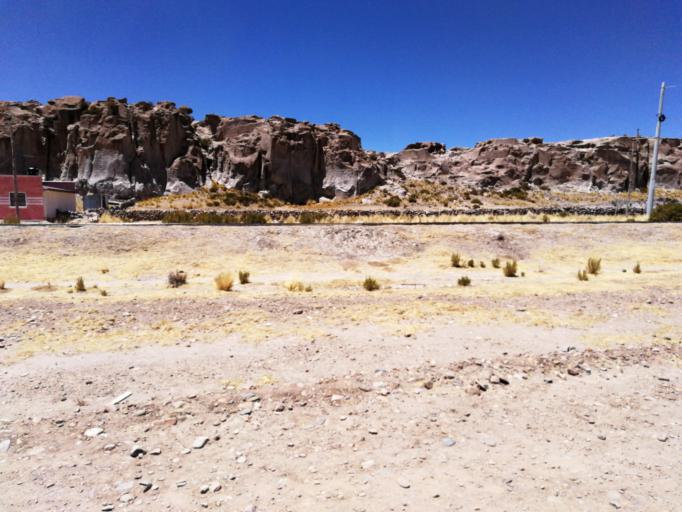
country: BO
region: Potosi
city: Colchani
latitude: -19.6922
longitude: -66.7767
